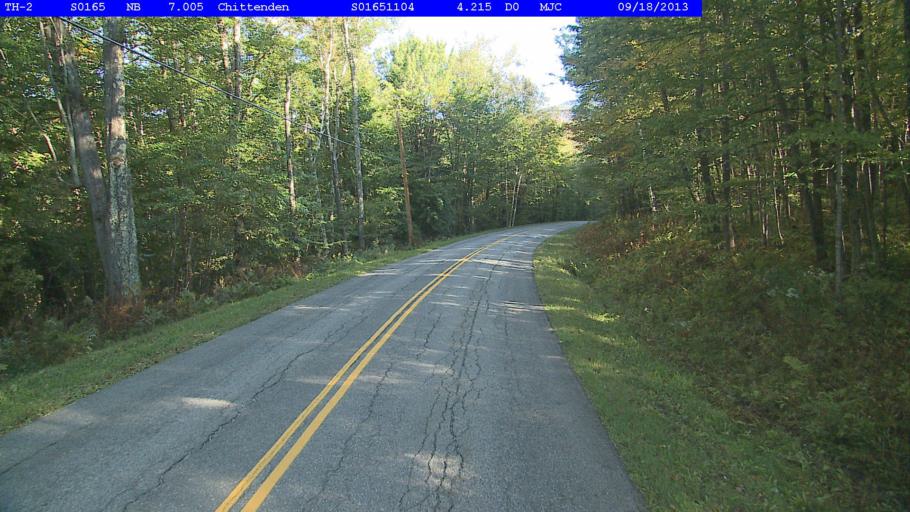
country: US
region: Vermont
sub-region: Rutland County
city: Rutland
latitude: 43.7347
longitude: -72.9718
